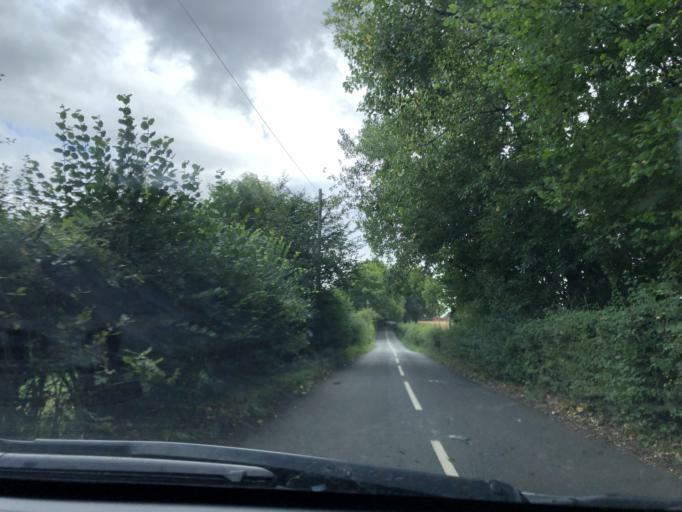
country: GB
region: England
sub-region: Kent
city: Westerham
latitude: 51.2339
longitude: 0.0882
